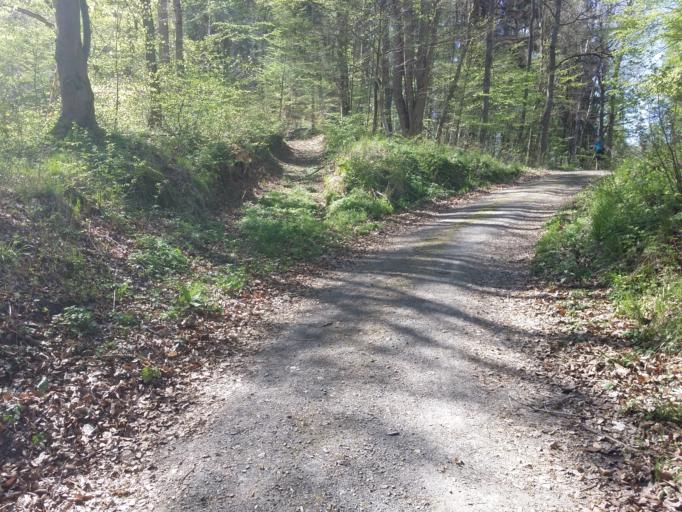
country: DE
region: Saxony-Anhalt
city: Harzgerode
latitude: 51.6726
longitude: 11.1900
